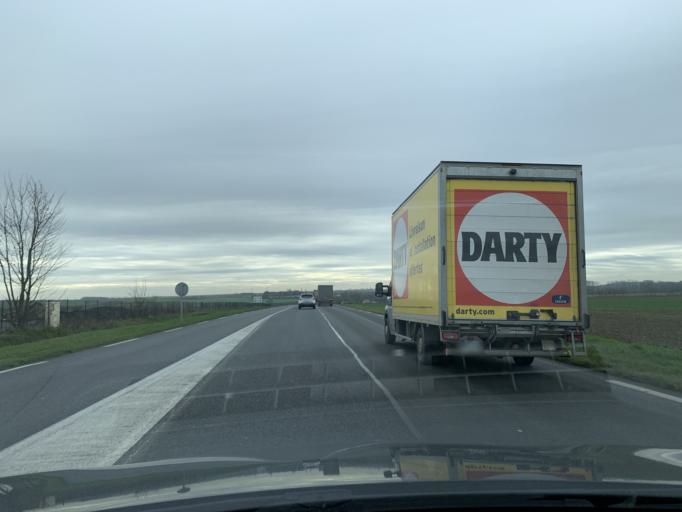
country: FR
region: Nord-Pas-de-Calais
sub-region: Departement du Nord
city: Aubigny-au-Bac
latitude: 50.2821
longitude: 3.1561
